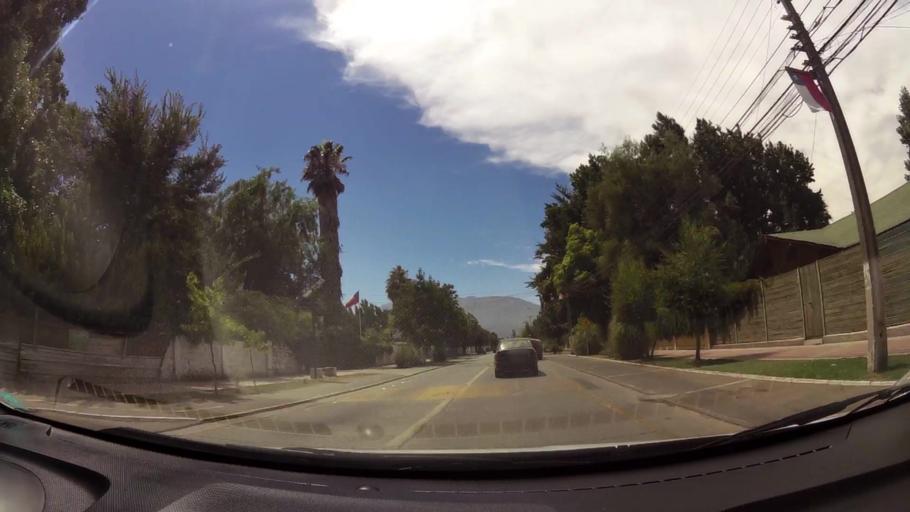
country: CL
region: O'Higgins
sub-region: Provincia de Cachapoal
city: Graneros
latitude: -33.9780
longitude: -70.7098
